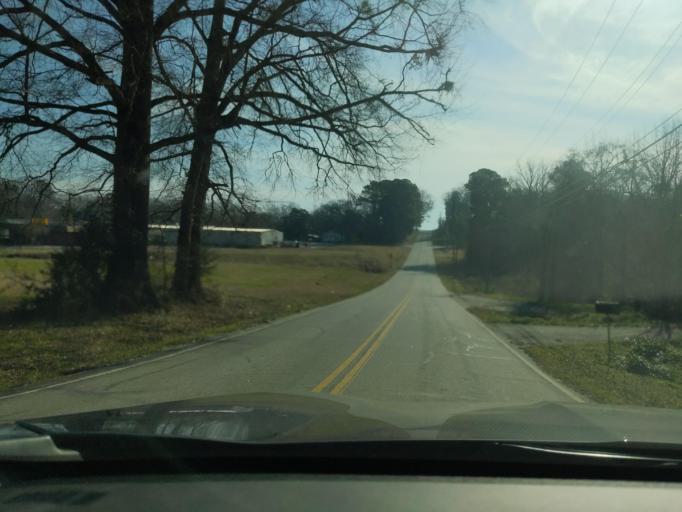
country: US
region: South Carolina
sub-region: Abbeville County
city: Calhoun Falls
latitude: 34.0904
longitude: -82.5945
